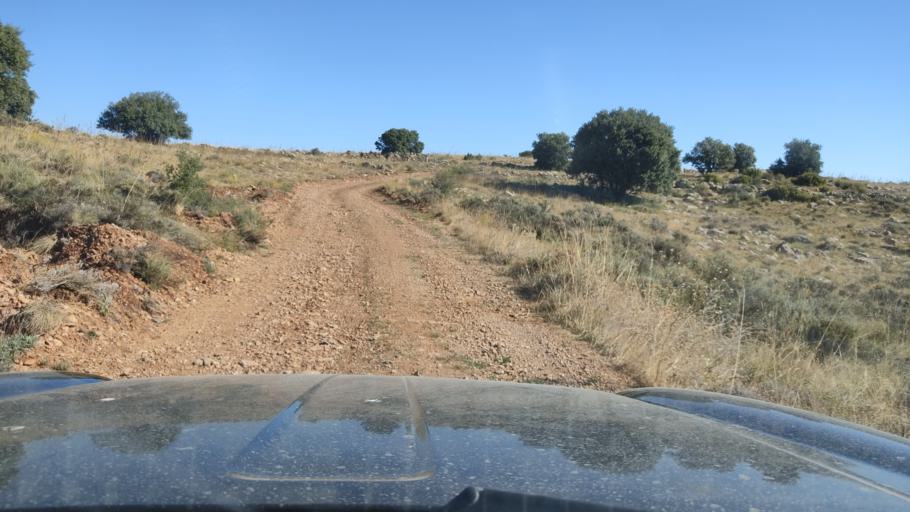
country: ES
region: Aragon
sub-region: Provincia de Teruel
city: Monforte de Moyuela
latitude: 41.0266
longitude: -1.0049
